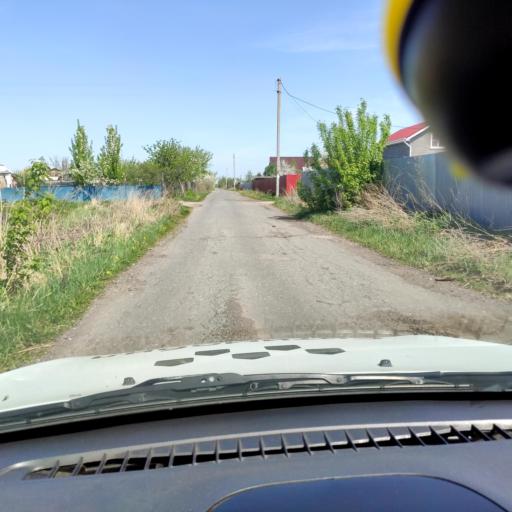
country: RU
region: Samara
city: Tol'yatti
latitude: 53.6665
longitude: 49.3628
